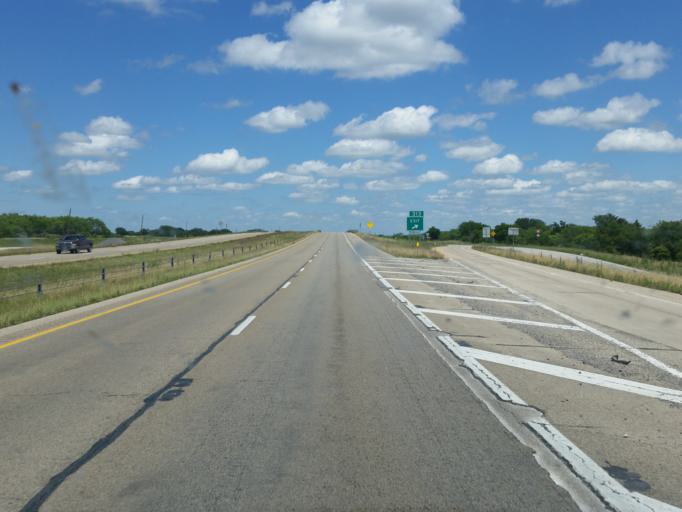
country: US
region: Texas
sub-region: Callahan County
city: Baird
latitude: 32.3863
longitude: -99.3023
